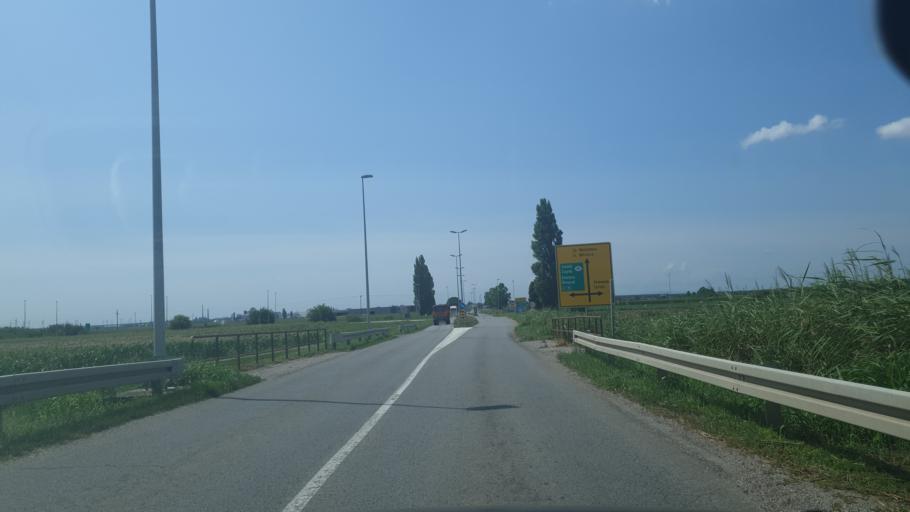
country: RS
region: Autonomna Pokrajina Vojvodina
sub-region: Sremski Okrug
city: Sremska Mitrovica
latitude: 44.9972
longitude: 19.6418
